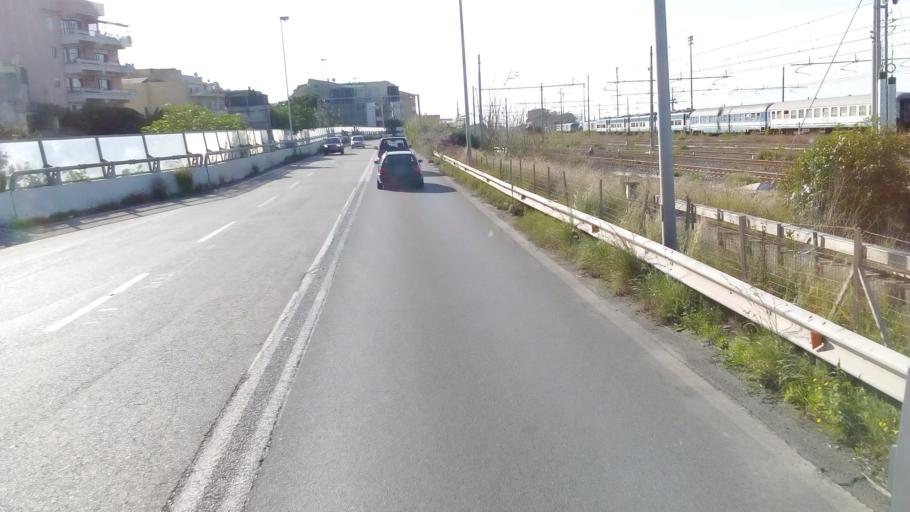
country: IT
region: Calabria
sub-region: Provincia di Reggio Calabria
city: Campo Calabro
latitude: 38.2111
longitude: 15.6354
